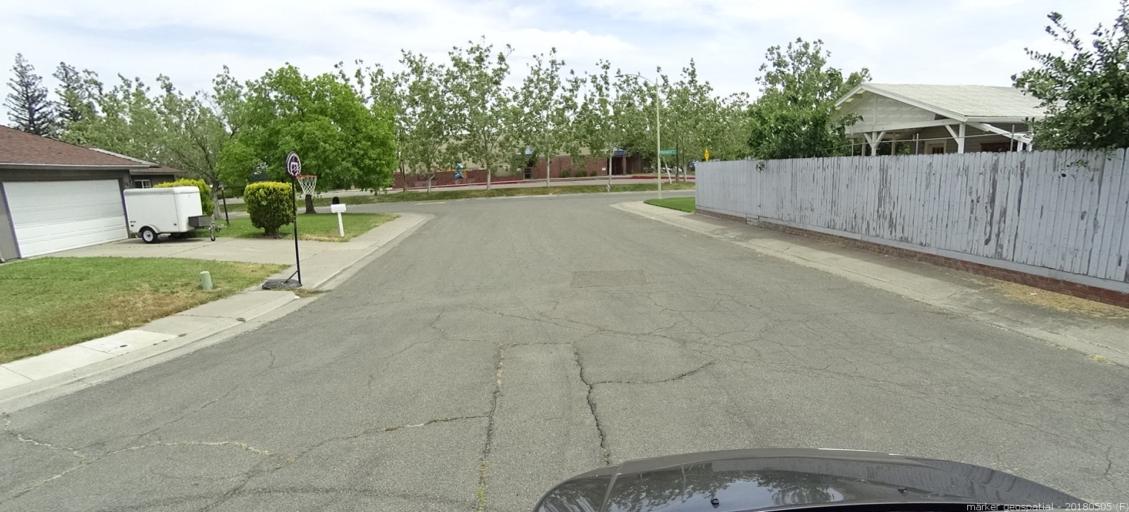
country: US
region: California
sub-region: Sacramento County
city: Rio Linda
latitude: 38.6446
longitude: -121.4644
